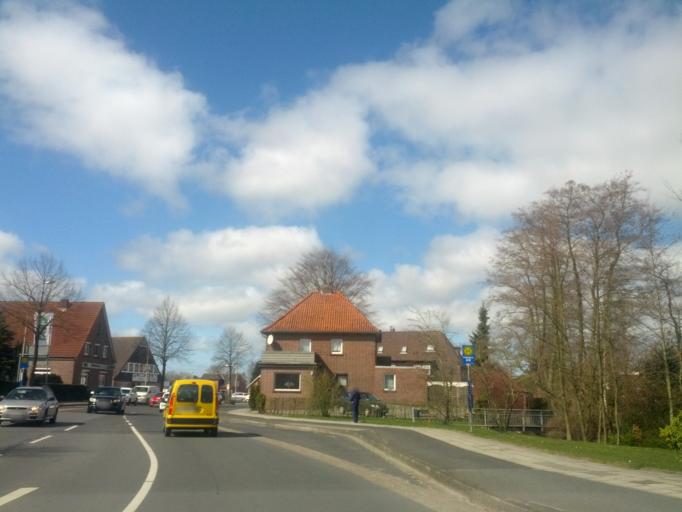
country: DE
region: Lower Saxony
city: Esens
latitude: 53.6430
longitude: 7.6121
